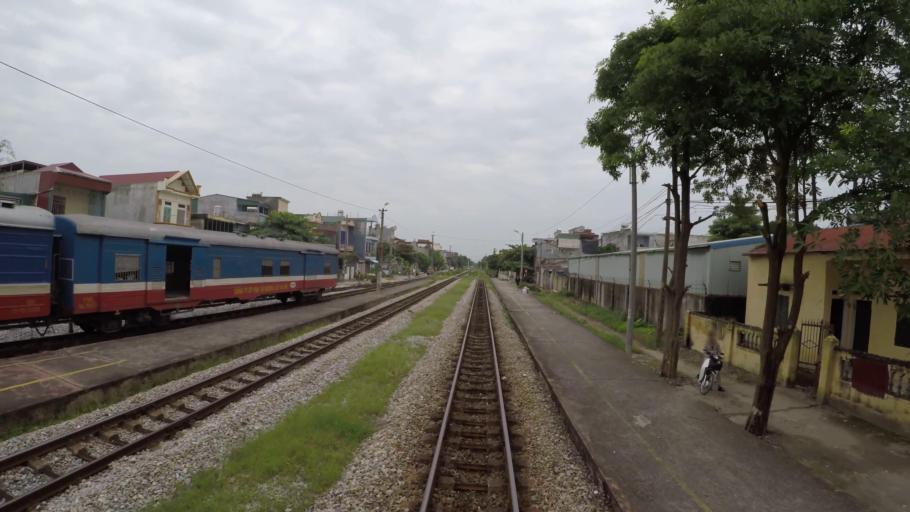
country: VN
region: Hai Duong
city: Thanh Pho Hai Duong
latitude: 20.9426
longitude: 106.3025
